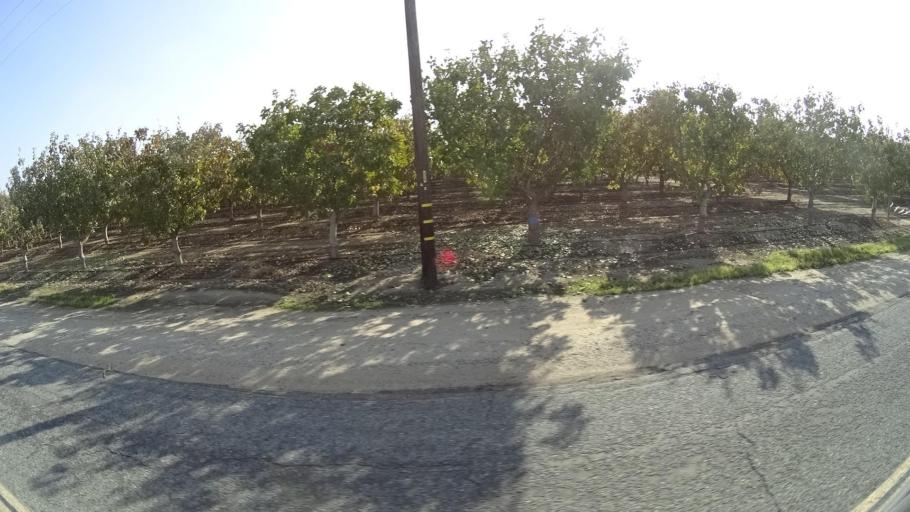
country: US
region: California
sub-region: Tulare County
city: Richgrove
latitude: 35.7908
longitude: -119.1046
